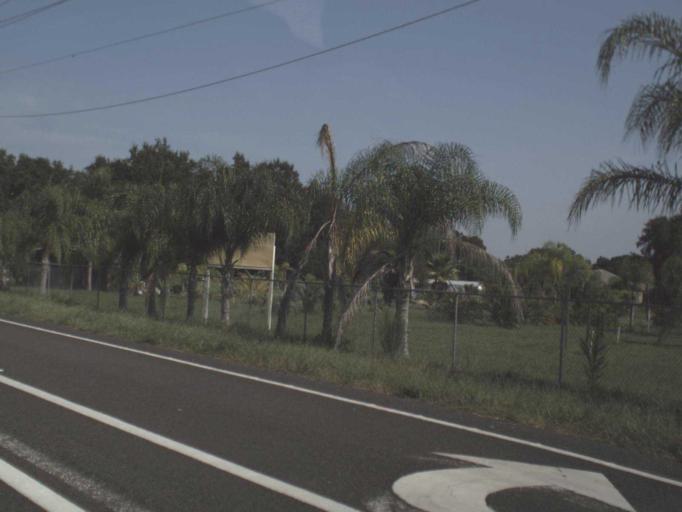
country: US
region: Florida
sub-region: Polk County
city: Willow Oak
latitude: 27.9365
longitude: -82.0878
